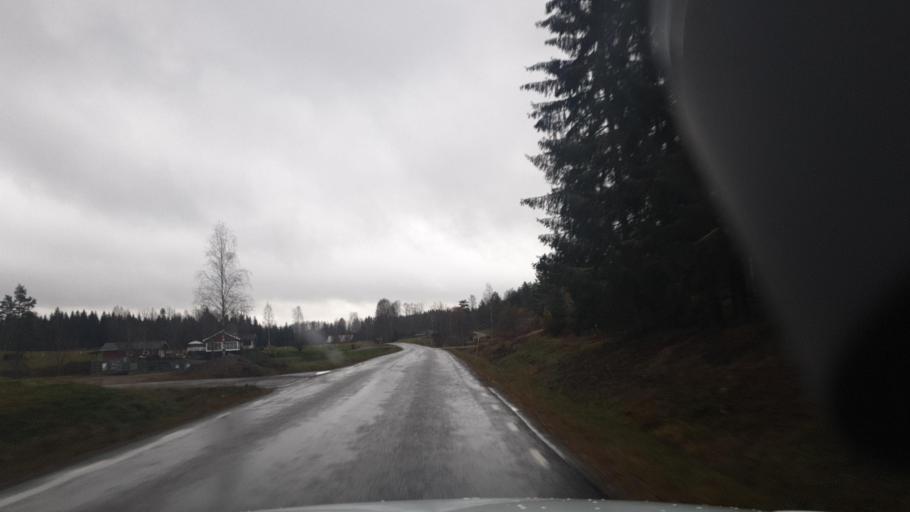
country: SE
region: Vaermland
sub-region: Eda Kommun
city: Charlottenberg
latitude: 59.7966
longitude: 12.1537
